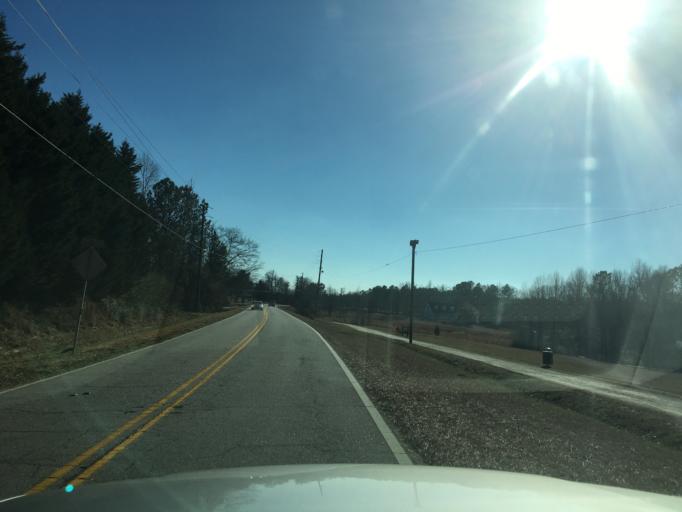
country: US
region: Georgia
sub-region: Carroll County
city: Villa Rica
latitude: 33.7073
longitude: -84.8613
